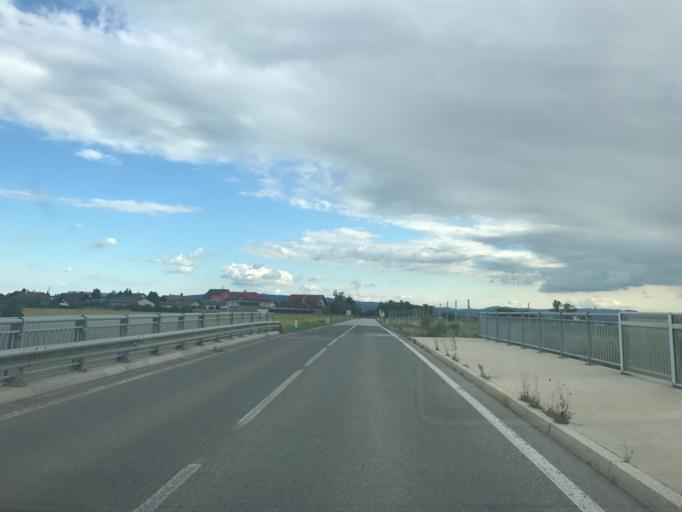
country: AT
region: Lower Austria
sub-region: Politischer Bezirk Wiener Neustadt
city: Theresienfeld
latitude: 47.8484
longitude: 16.2325
